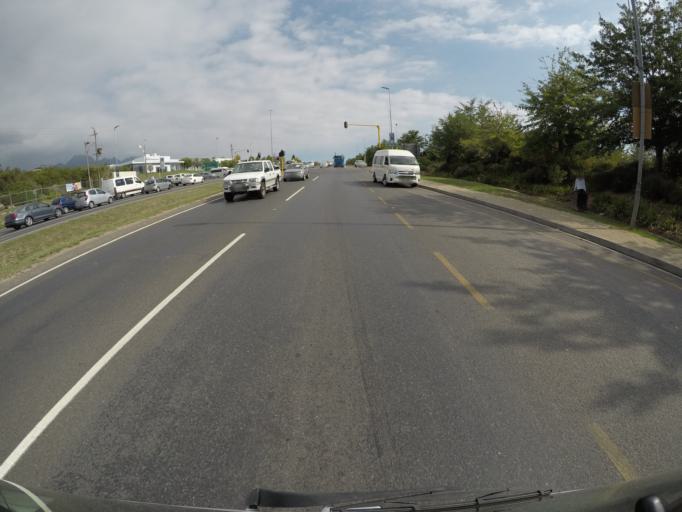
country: ZA
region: Western Cape
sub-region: Cape Winelands District Municipality
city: Stellenbosch
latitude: -33.9744
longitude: 18.8420
